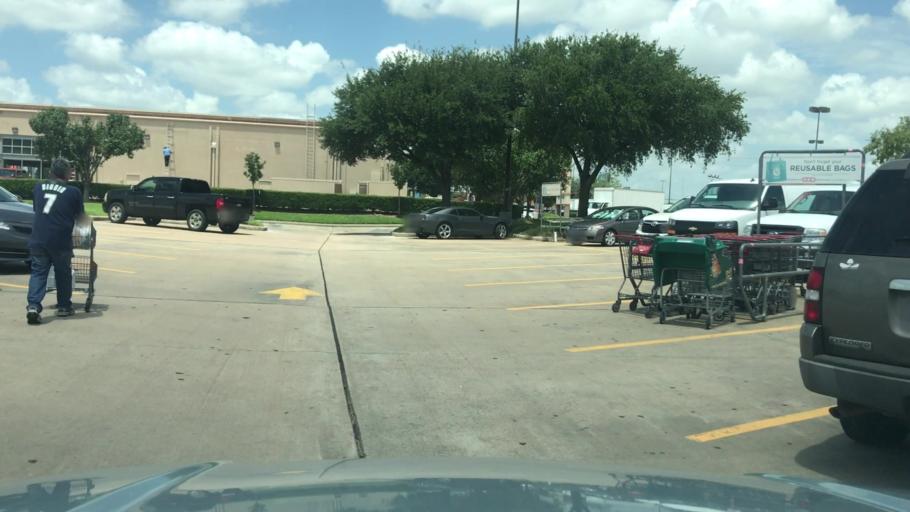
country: US
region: Texas
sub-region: Fort Bend County
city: Cinco Ranch
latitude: 29.7887
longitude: -95.7174
